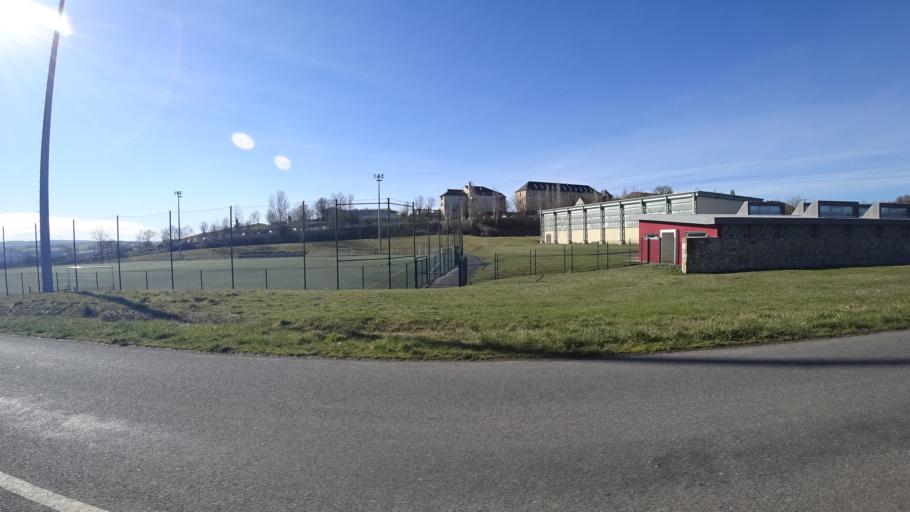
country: FR
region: Midi-Pyrenees
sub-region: Departement de l'Aveyron
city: Sebazac-Concoures
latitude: 44.3838
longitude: 2.5876
